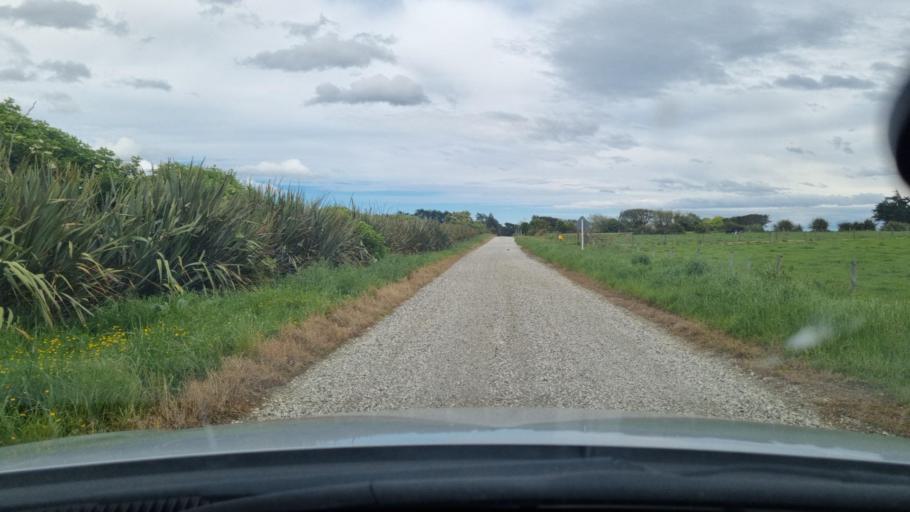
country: NZ
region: Southland
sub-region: Invercargill City
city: Invercargill
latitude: -46.4026
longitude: 168.2593
